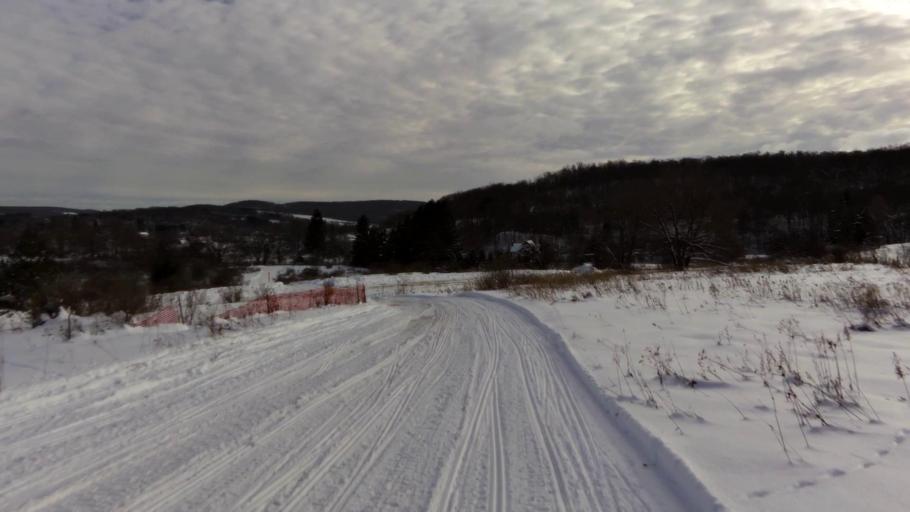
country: US
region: New York
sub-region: Cattaraugus County
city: Franklinville
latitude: 42.3395
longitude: -78.4742
